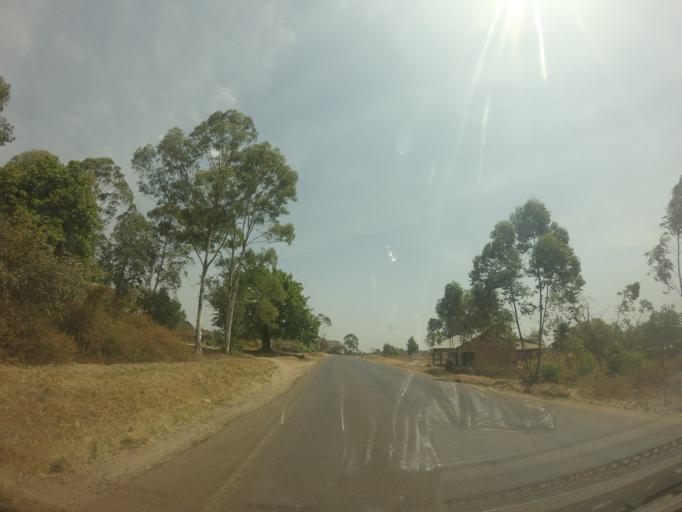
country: UG
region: Northern Region
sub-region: Arua District
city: Arua
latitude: 2.9565
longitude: 30.9228
